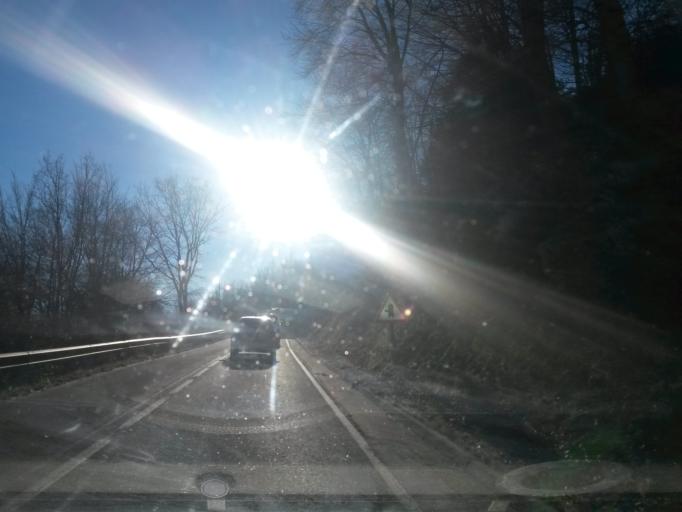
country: ES
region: Catalonia
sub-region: Provincia de Girona
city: Sant Feliu de Pallerols
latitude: 42.0485
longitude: 2.5108
